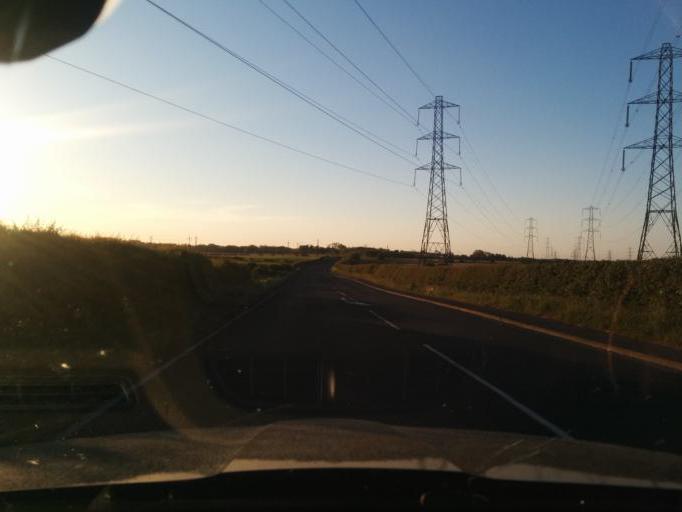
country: GB
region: England
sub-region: Northumberland
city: Bedlington
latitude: 55.1154
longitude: -1.5733
